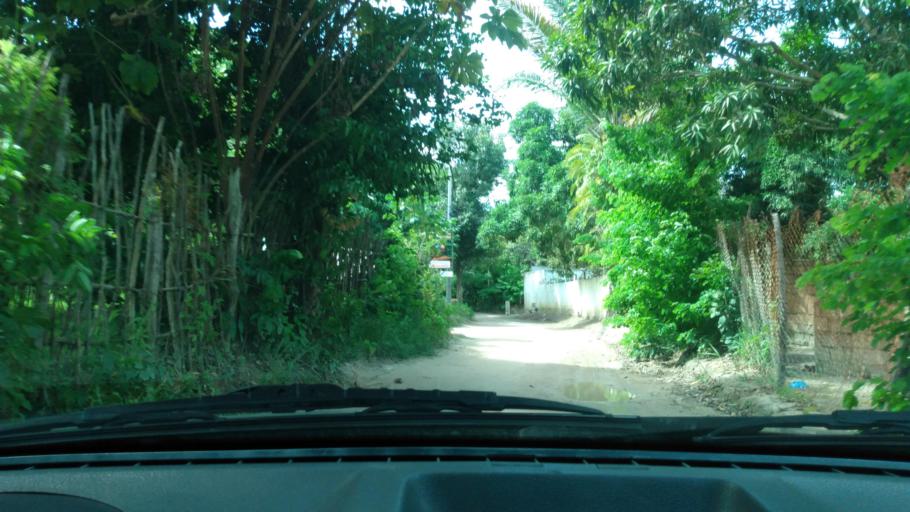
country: BR
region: Pernambuco
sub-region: Cabo De Santo Agostinho
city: Cabo
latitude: -8.3534
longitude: -34.9647
